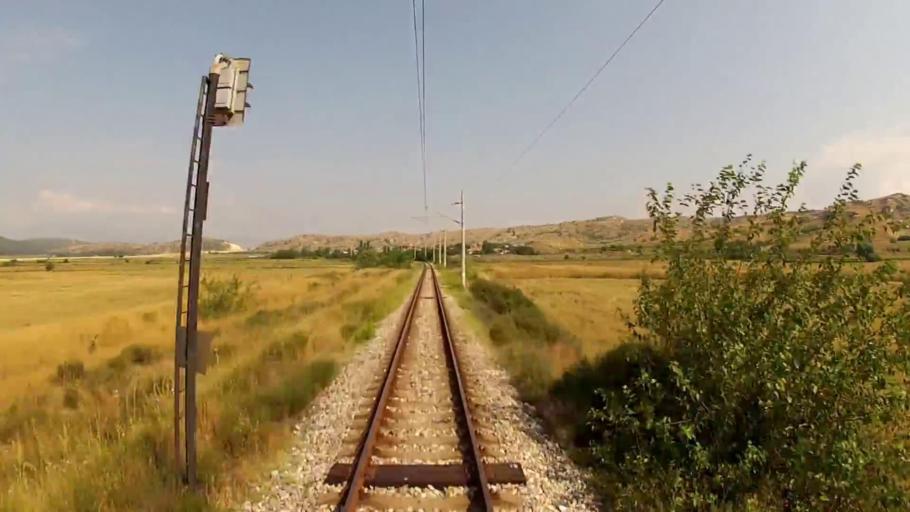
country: BG
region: Blagoevgrad
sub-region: Obshtina Petrich
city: Petrich
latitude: 41.4143
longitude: 23.3426
